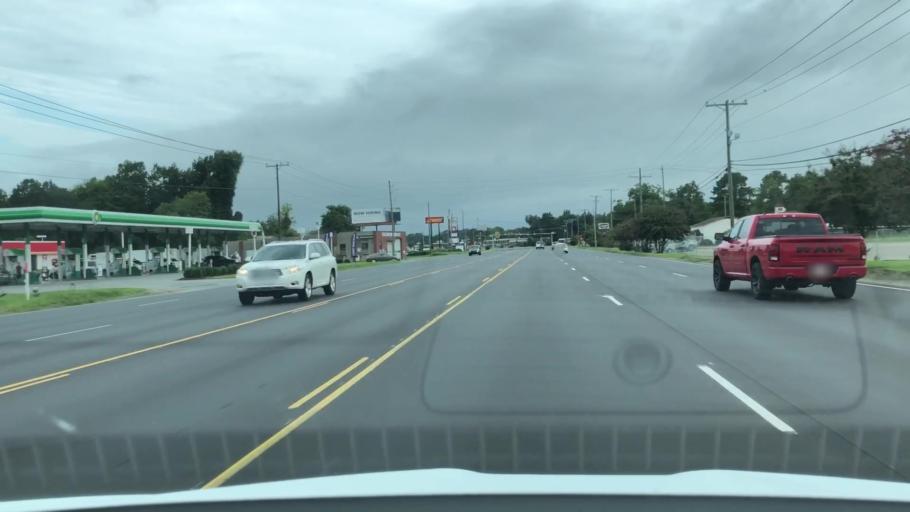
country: US
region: North Carolina
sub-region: Lenoir County
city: Kinston
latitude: 35.2393
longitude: -77.5759
